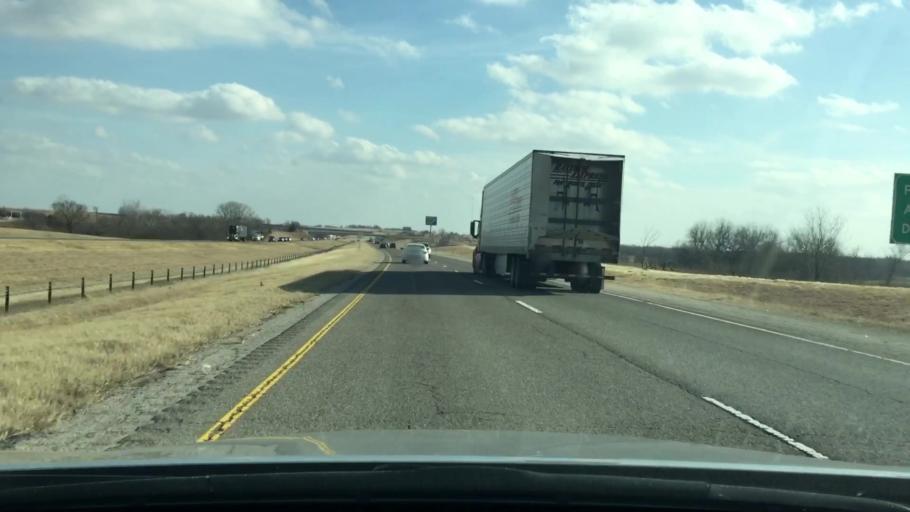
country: US
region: Oklahoma
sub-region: Garvin County
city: Maysville
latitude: 34.9021
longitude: -97.3499
